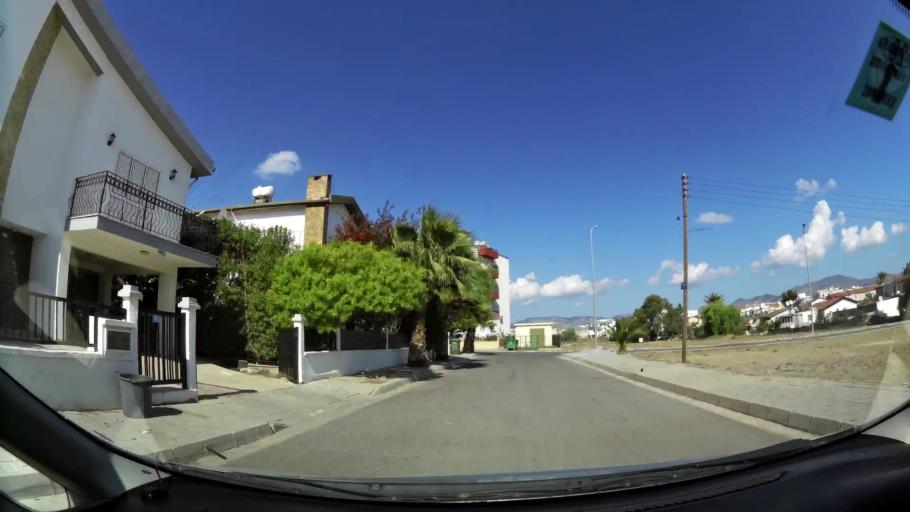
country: CY
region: Lefkosia
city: Nicosia
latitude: 35.2056
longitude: 33.3356
